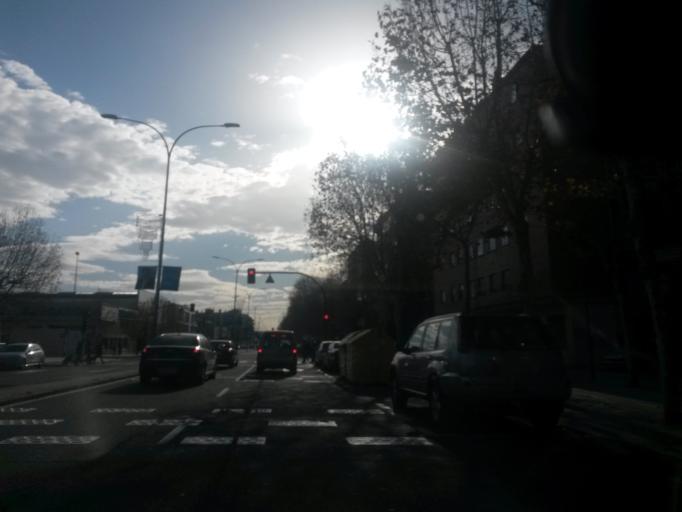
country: ES
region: Castille and Leon
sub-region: Provincia de Salamanca
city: Salamanca
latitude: 40.9769
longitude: -5.6494
